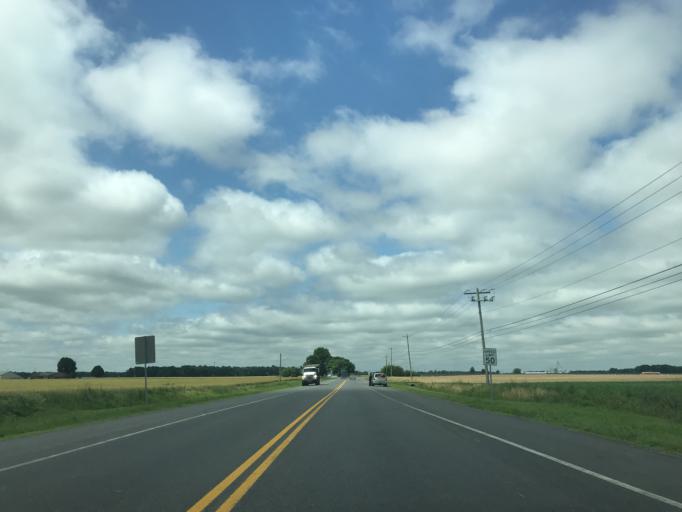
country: US
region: Maryland
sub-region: Caroline County
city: Ridgely
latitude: 38.9376
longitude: -75.8906
